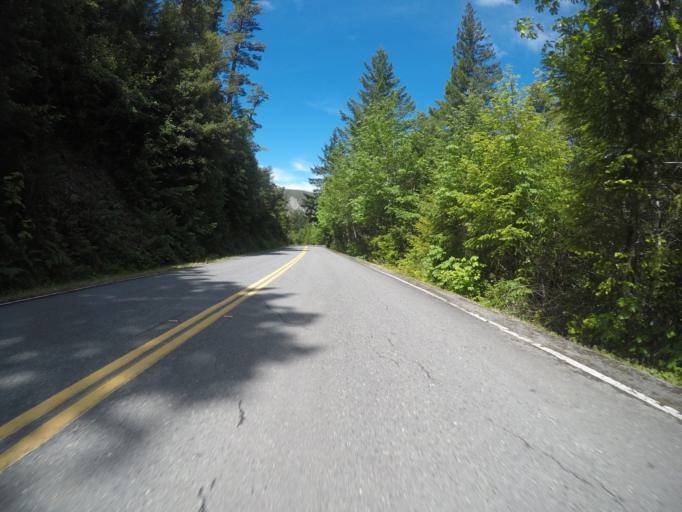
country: US
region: California
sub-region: Del Norte County
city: Bertsch-Oceanview
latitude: 41.7266
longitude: -123.9615
